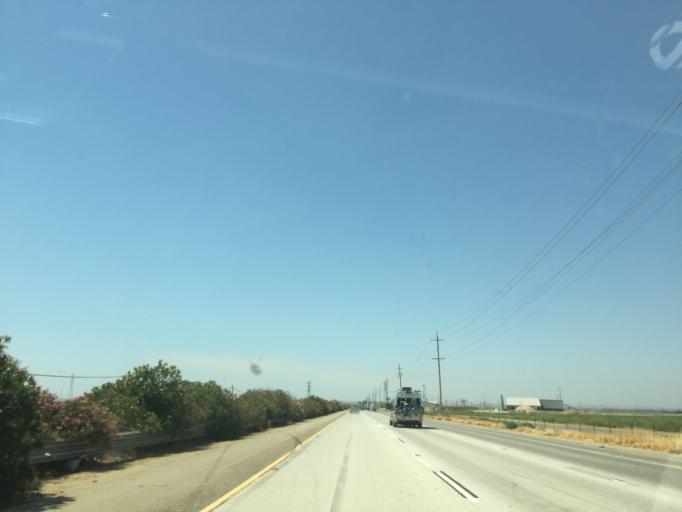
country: US
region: California
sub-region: Kern County
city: Weedpatch
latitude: 35.0800
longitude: -118.9748
